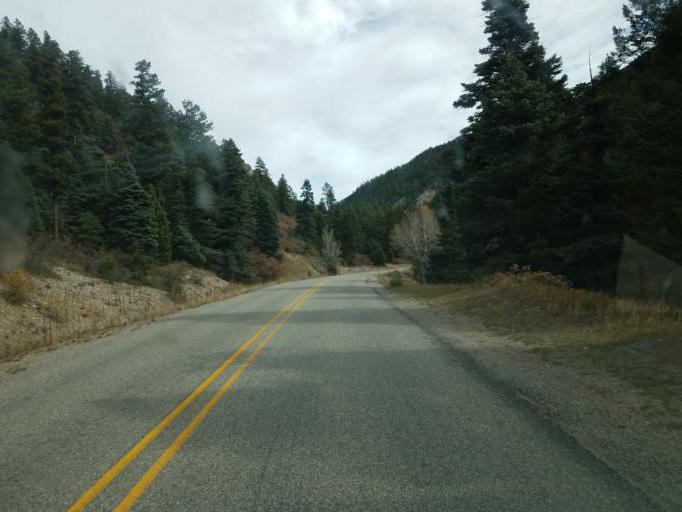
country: US
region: New Mexico
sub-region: Taos County
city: Arroyo Seco
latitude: 36.5606
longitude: -105.5338
